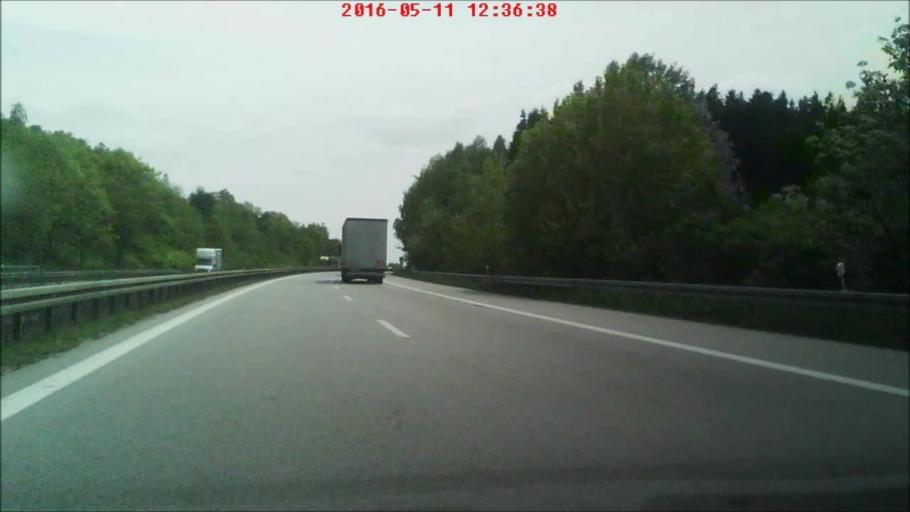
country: DE
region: Bavaria
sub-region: Lower Bavaria
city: Aicha vorm Wald
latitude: 48.6465
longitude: 13.2862
